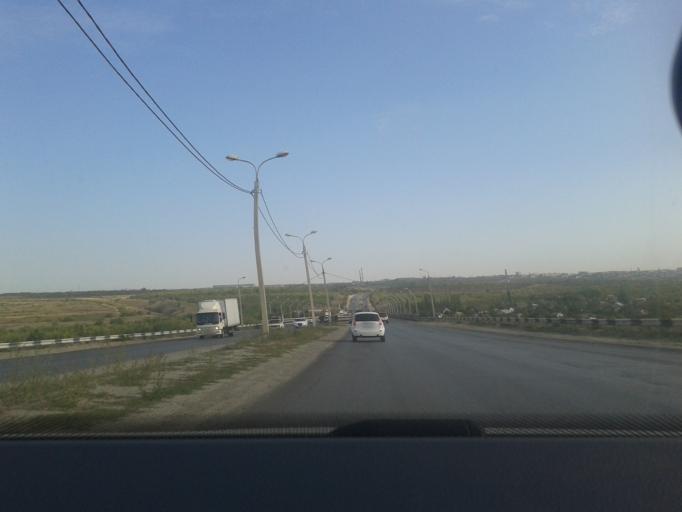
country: RU
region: Volgograd
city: Volgograd
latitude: 48.7131
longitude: 44.4433
